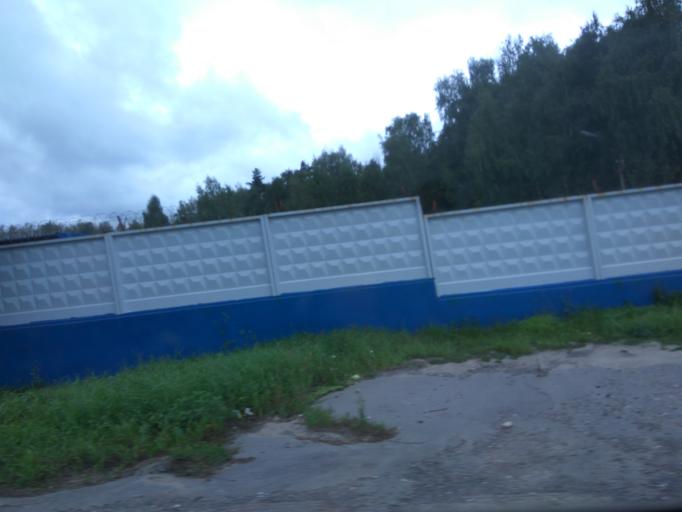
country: RU
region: Moskovskaya
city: Malyshevo
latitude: 55.5178
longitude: 38.3420
